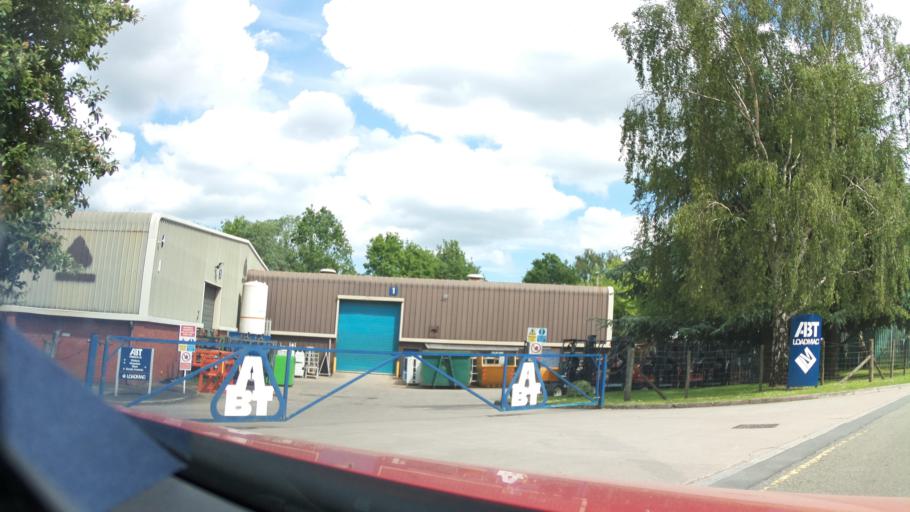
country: GB
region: England
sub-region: Herefordshire
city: Ross on Wye
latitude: 51.9164
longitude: -2.5716
